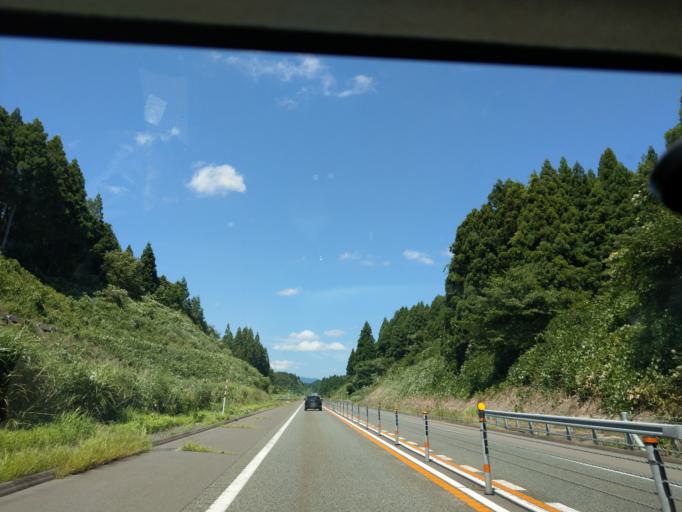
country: JP
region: Akita
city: Akita
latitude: 39.6890
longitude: 140.1857
